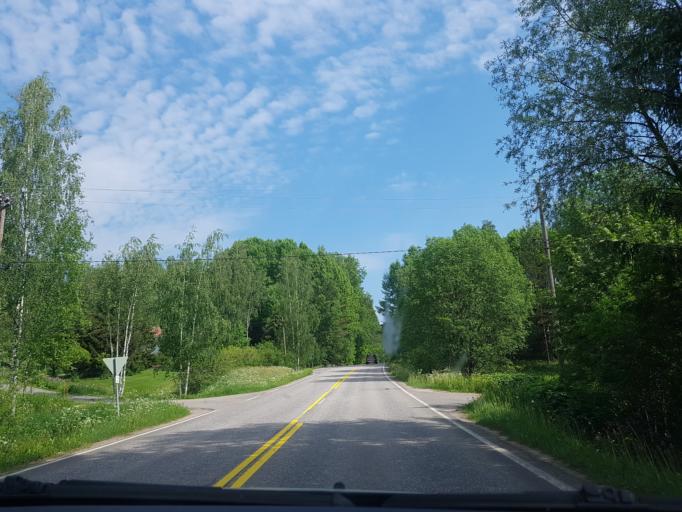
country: FI
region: Uusimaa
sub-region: Helsinki
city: Vihti
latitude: 60.2974
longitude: 24.3987
